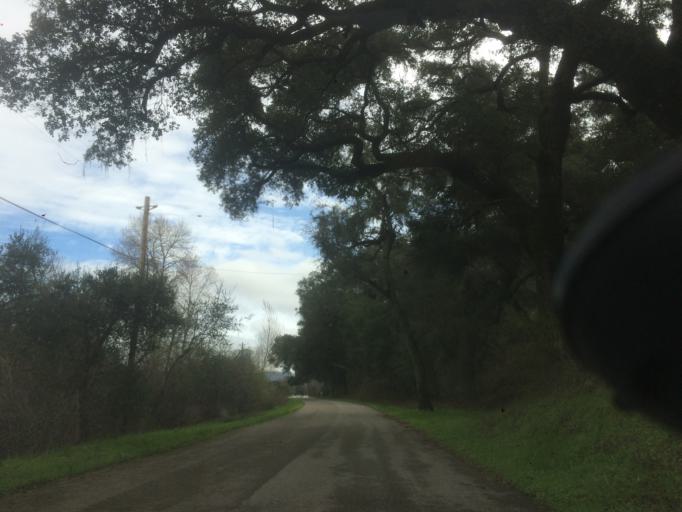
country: US
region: California
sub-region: San Luis Obispo County
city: Nipomo
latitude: 35.2071
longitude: -120.4121
